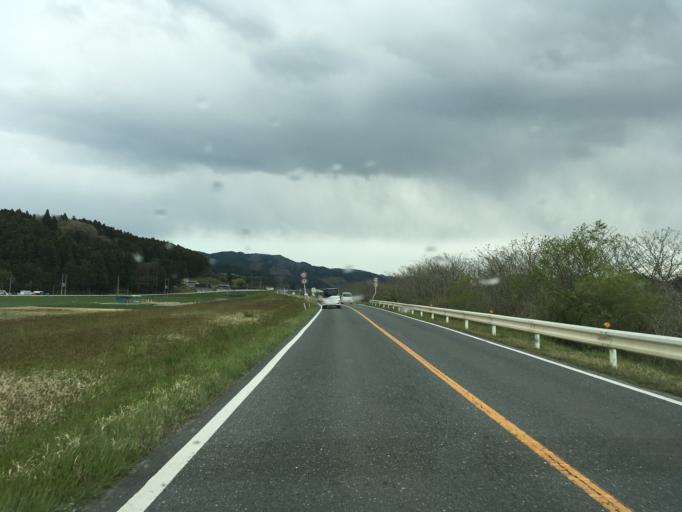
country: JP
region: Miyagi
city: Wakuya
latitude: 38.6289
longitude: 141.2925
